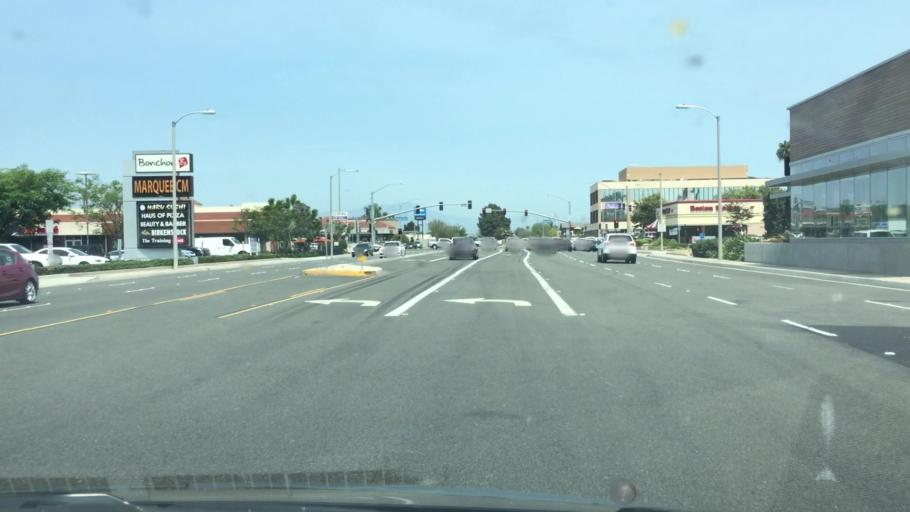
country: US
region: California
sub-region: Orange County
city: Costa Mesa
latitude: 33.6733
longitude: -117.9211
